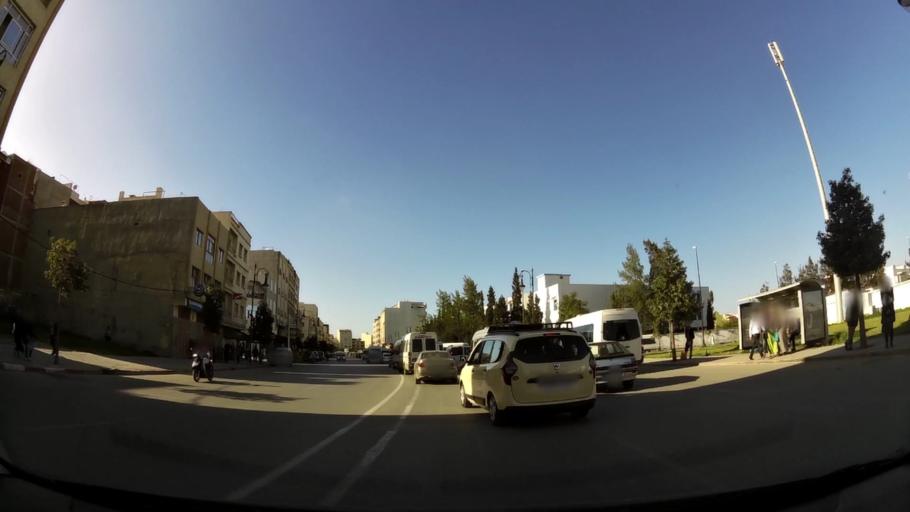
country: MA
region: Tanger-Tetouan
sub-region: Tanger-Assilah
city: Tangier
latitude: 35.7489
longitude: -5.7987
